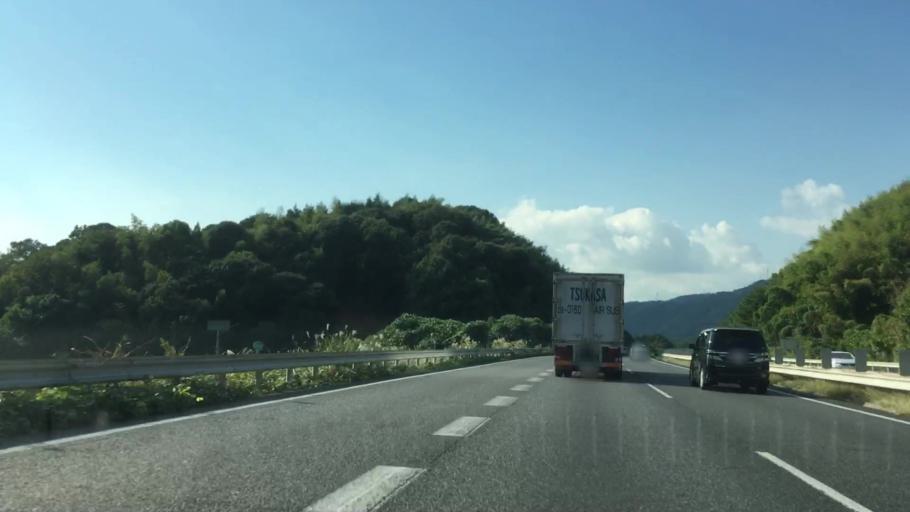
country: JP
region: Yamaguchi
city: Kudamatsu
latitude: 34.0332
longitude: 131.9316
